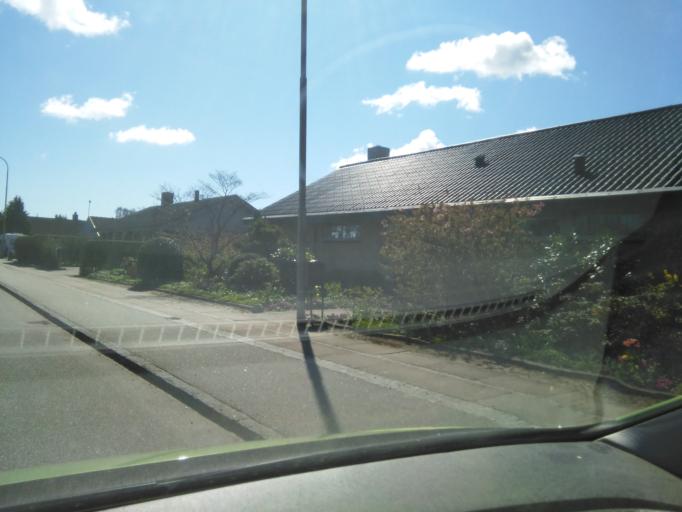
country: DK
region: Central Jutland
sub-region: Arhus Kommune
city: Lystrup
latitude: 56.2028
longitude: 10.2562
